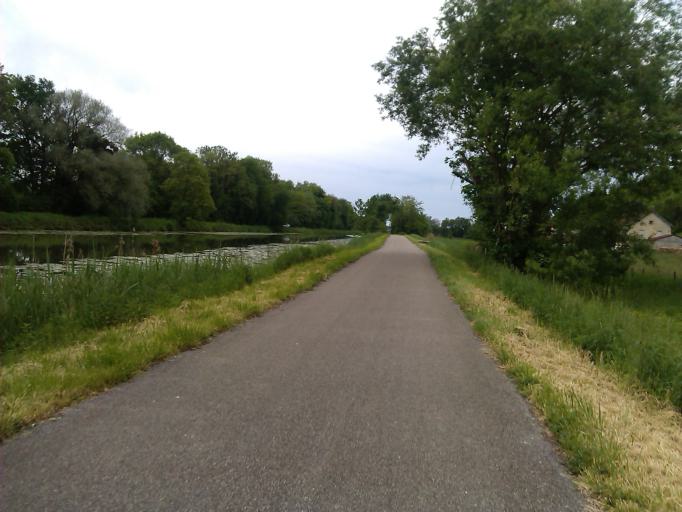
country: FR
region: Franche-Comte
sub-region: Departement du Jura
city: Choisey
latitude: 47.0698
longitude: 5.4676
